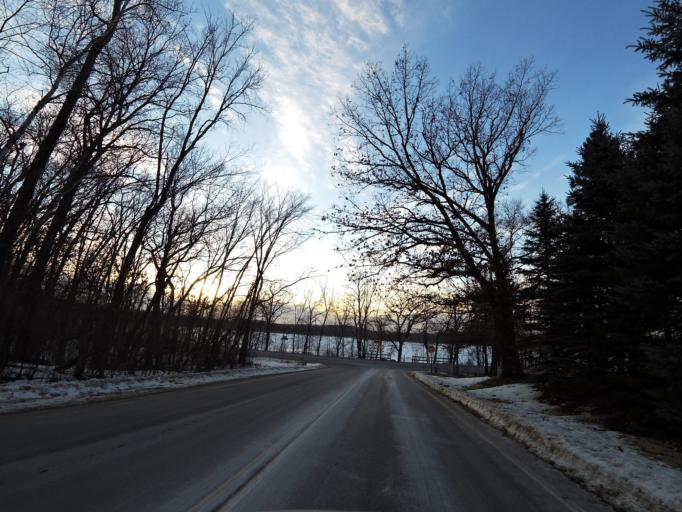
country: US
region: Minnesota
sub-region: Washington County
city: Lake Elmo
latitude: 44.9780
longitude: -92.8824
